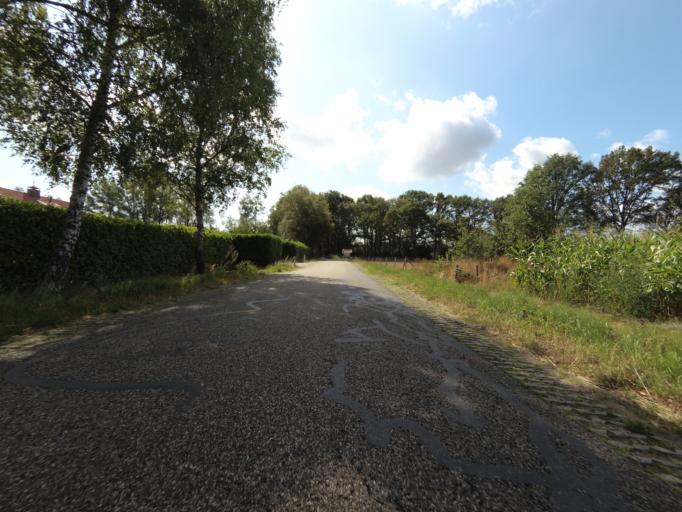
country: NL
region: Overijssel
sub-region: Gemeente Oldenzaal
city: Oldenzaal
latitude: 52.2985
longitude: 6.8811
